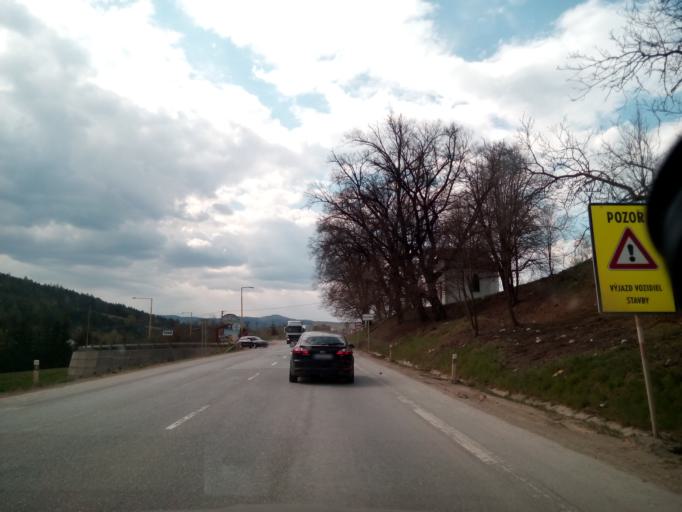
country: SK
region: Presovsky
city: Sabinov
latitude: 49.0205
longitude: 21.0322
